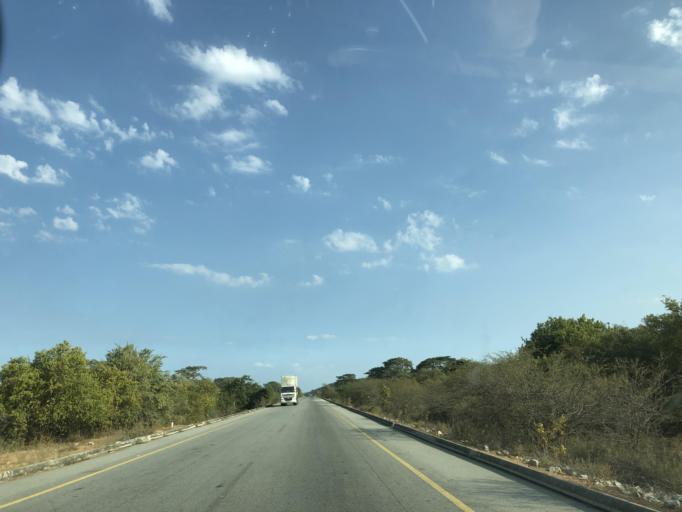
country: AO
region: Benguela
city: Benguela
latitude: -13.2452
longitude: 13.7744
